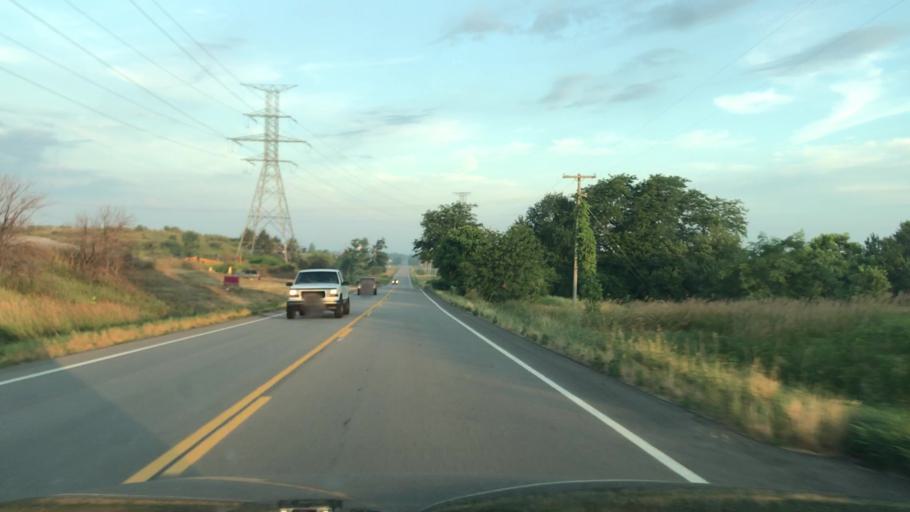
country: US
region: Michigan
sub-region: Ottawa County
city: Hudsonville
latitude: 42.7824
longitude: -85.9093
